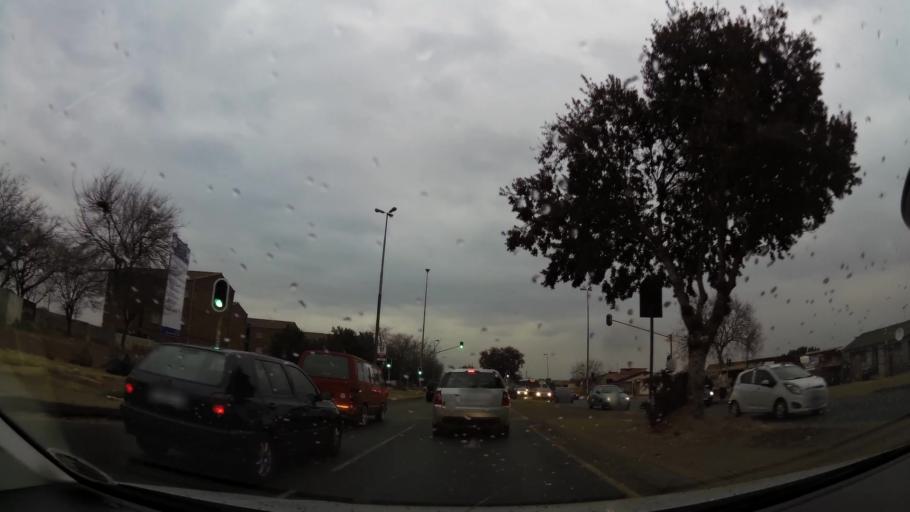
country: ZA
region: Gauteng
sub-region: City of Johannesburg Metropolitan Municipality
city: Soweto
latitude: -26.2545
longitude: 27.8547
